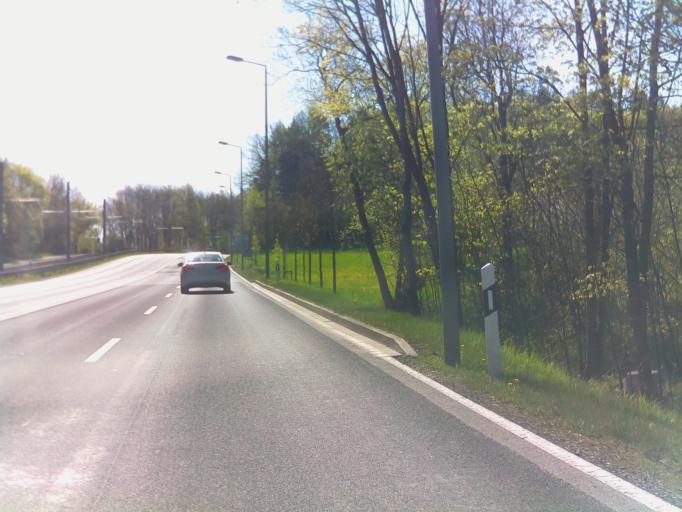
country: DE
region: Saxony
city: Plauen
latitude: 50.5206
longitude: 12.1157
